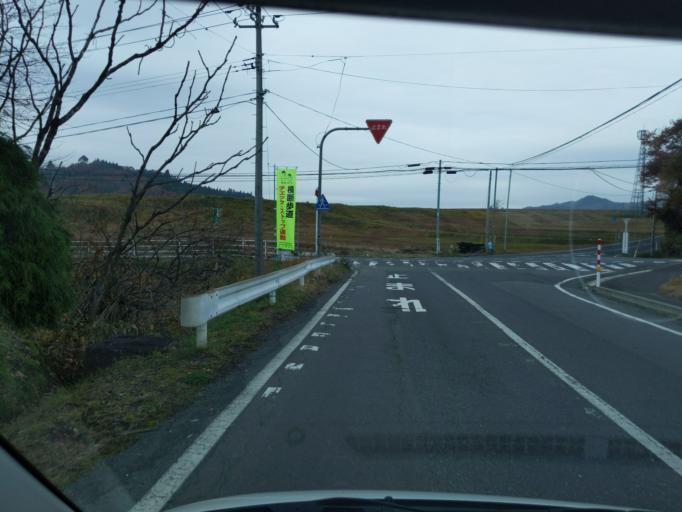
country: JP
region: Iwate
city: Kitakami
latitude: 39.2527
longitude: 141.2086
